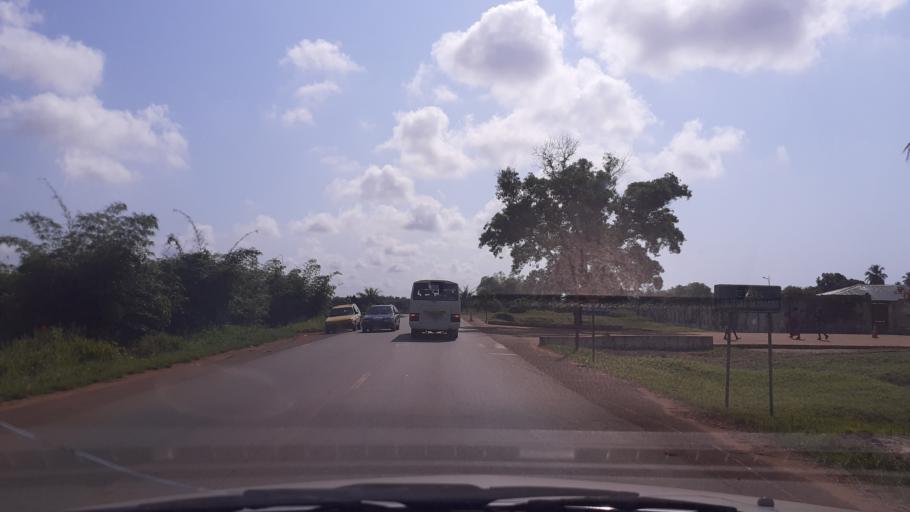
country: LR
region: Montserrado
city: Bensonville City
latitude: 6.2099
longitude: -10.5652
